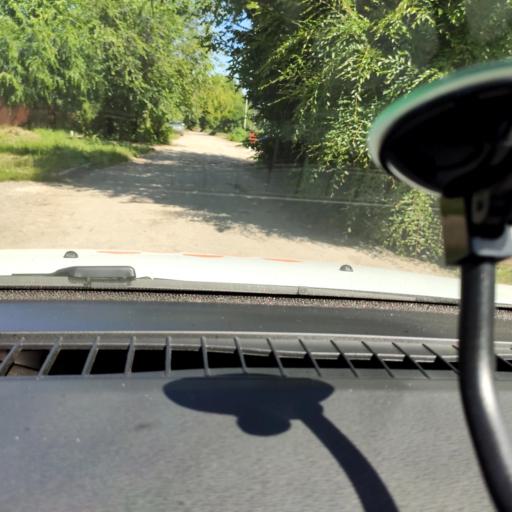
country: RU
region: Samara
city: Petra-Dubrava
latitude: 53.2517
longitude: 50.3335
